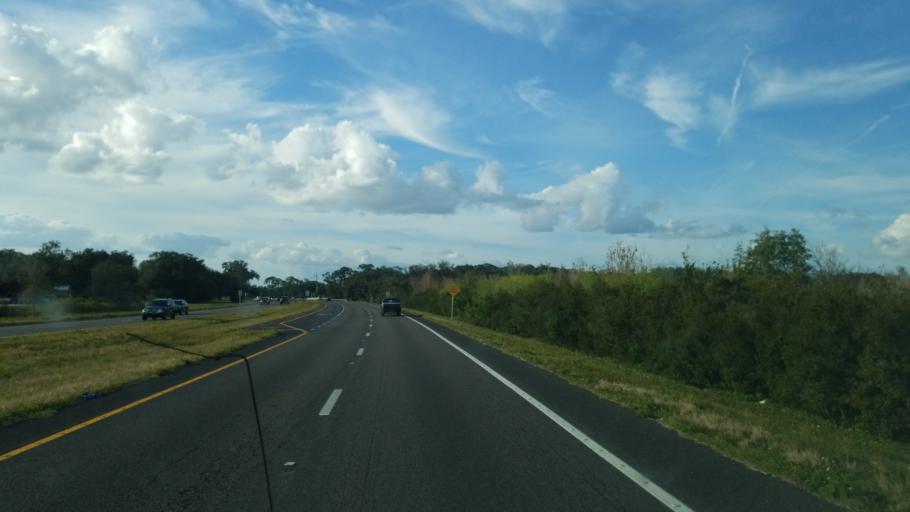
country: US
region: Florida
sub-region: Osceola County
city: Saint Cloud
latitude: 28.2324
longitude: -81.1866
